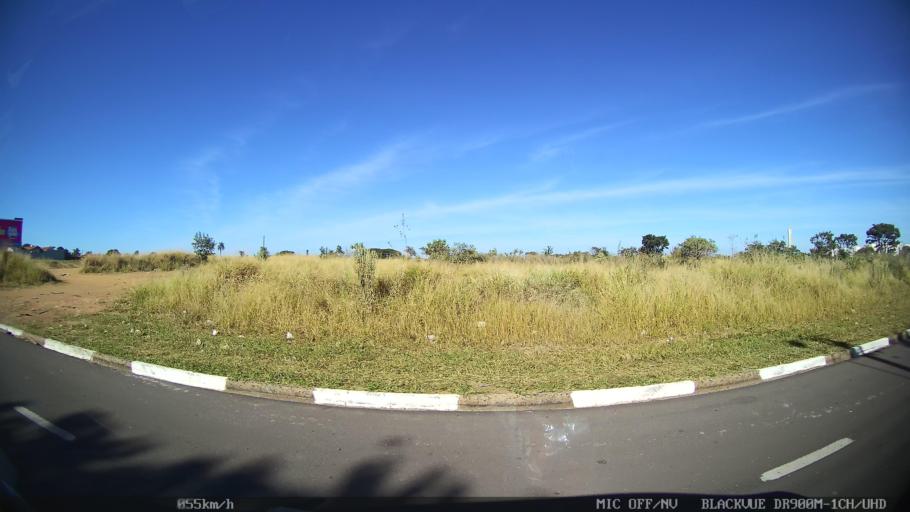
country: BR
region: Sao Paulo
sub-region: Franca
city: Franca
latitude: -20.5597
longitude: -47.3762
